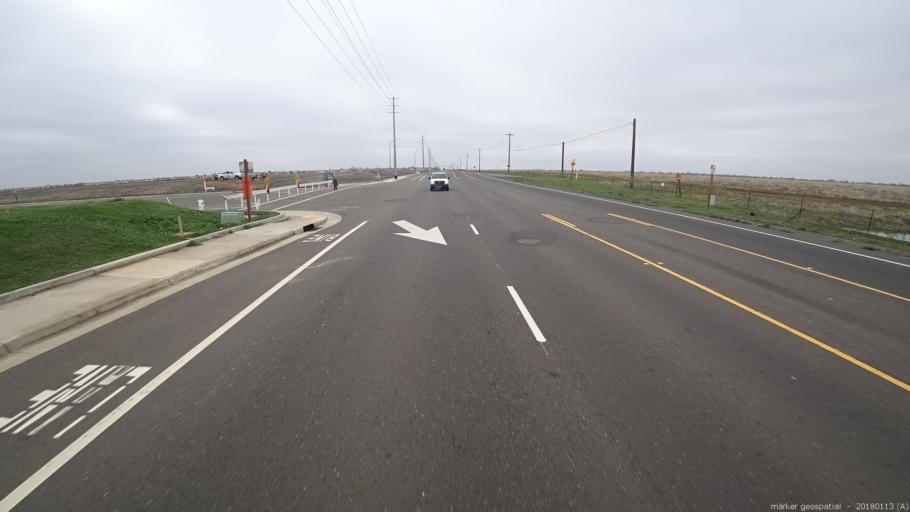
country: US
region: California
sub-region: Sacramento County
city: Gold River
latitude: 38.5592
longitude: -121.2239
